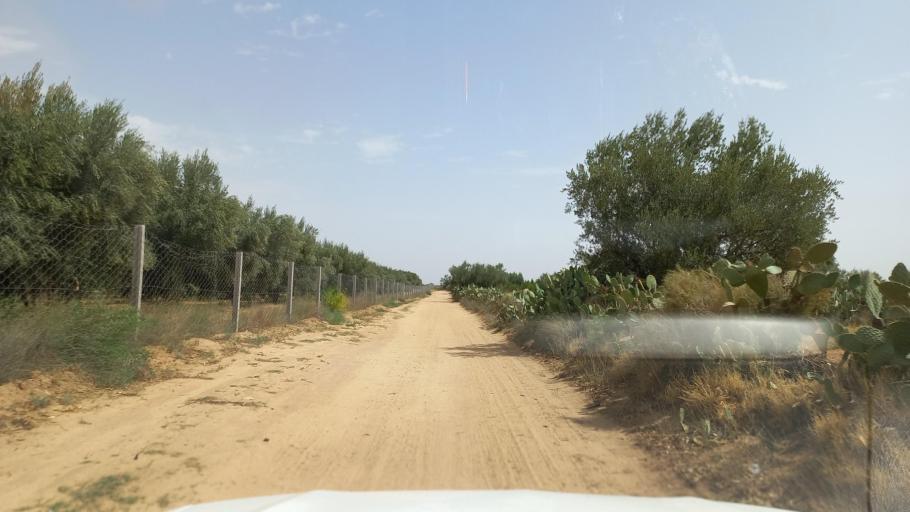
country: TN
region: Al Qasrayn
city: Kasserine
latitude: 35.2551
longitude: 9.0554
